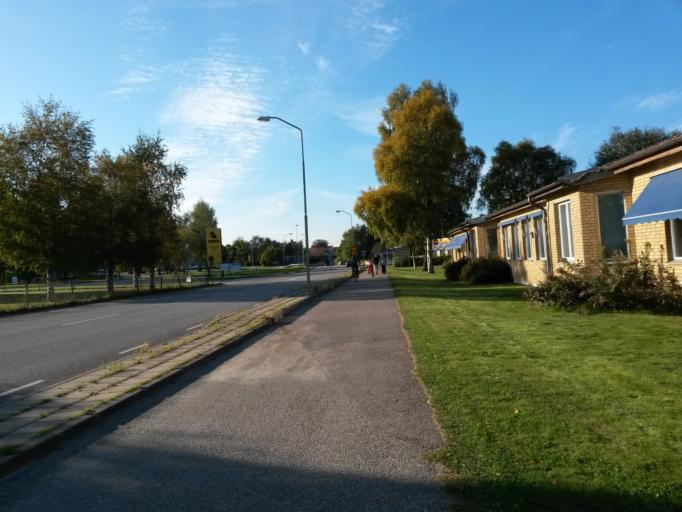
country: SE
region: Vaestra Goetaland
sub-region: Herrljunga Kommun
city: Herrljunga
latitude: 58.0761
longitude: 13.0174
